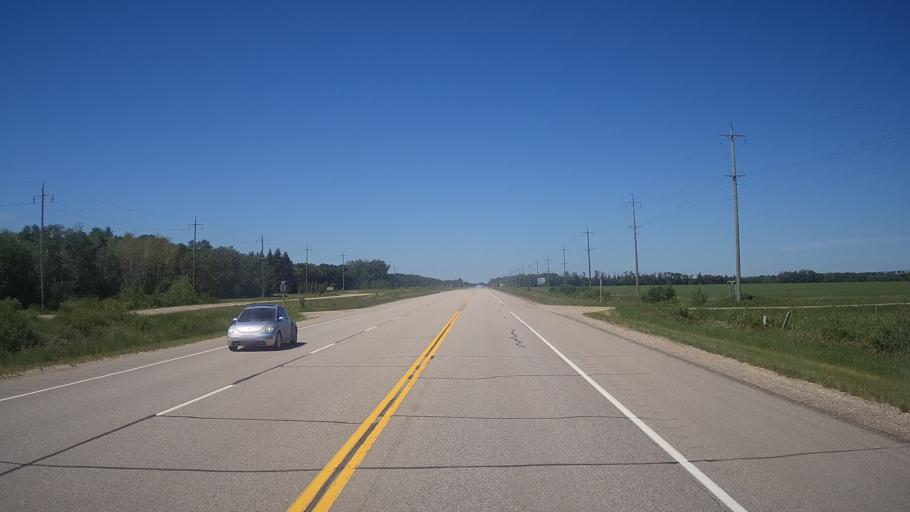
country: CA
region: Manitoba
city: Neepawa
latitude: 50.2253
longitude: -99.3388
